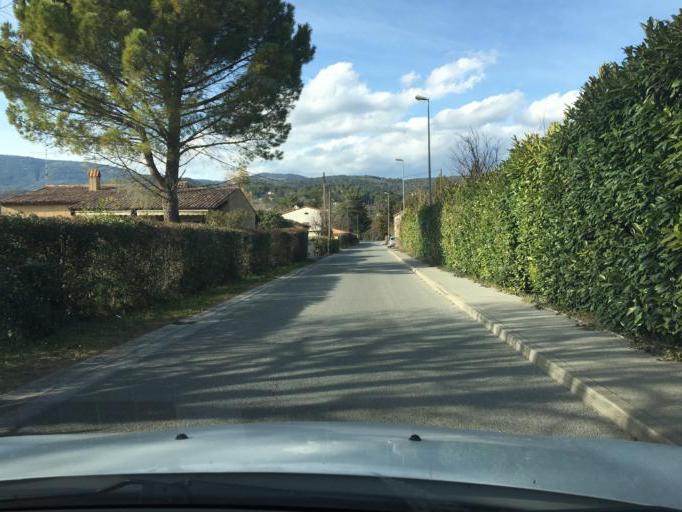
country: FR
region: Provence-Alpes-Cote d'Azur
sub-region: Departement du Var
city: Fayence
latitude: 43.6239
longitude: 6.6887
